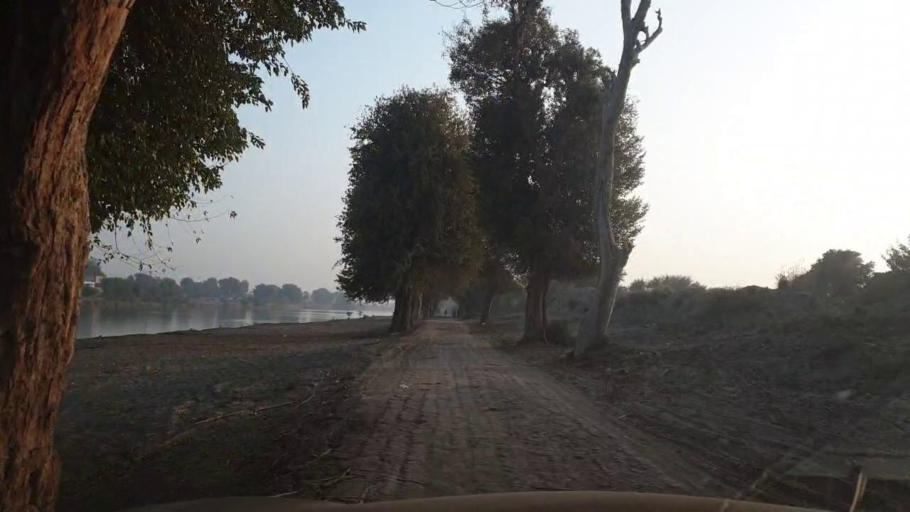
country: PK
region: Sindh
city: Ubauro
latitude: 28.3128
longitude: 69.7898
